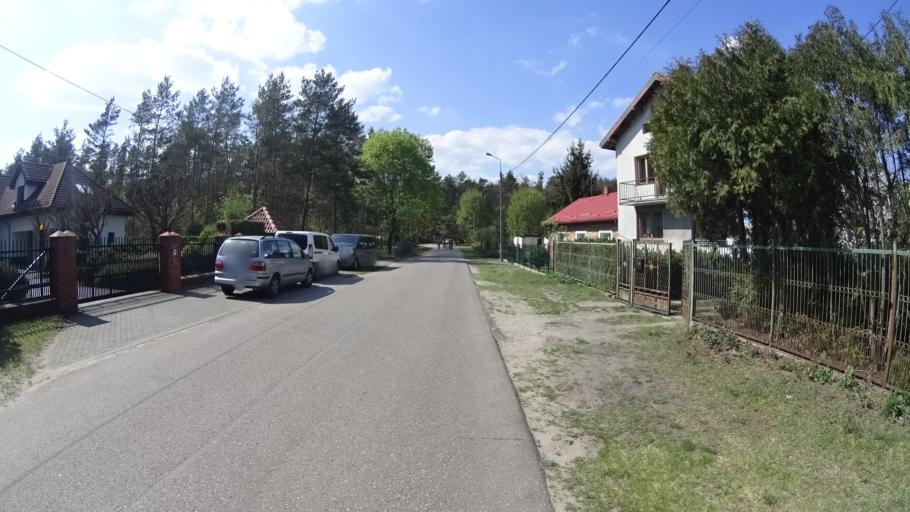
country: PL
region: Masovian Voivodeship
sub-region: Powiat warszawski zachodni
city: Truskaw
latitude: 52.3175
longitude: 20.7987
